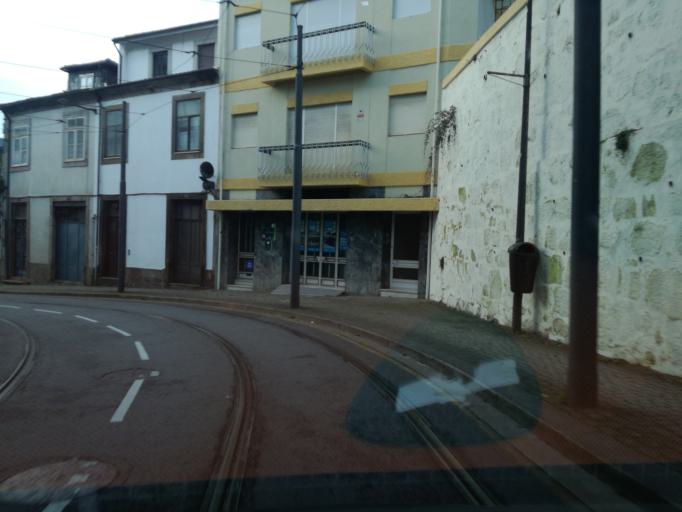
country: PT
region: Porto
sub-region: Vila Nova de Gaia
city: Vila Nova de Gaia
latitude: 41.1464
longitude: -8.6296
